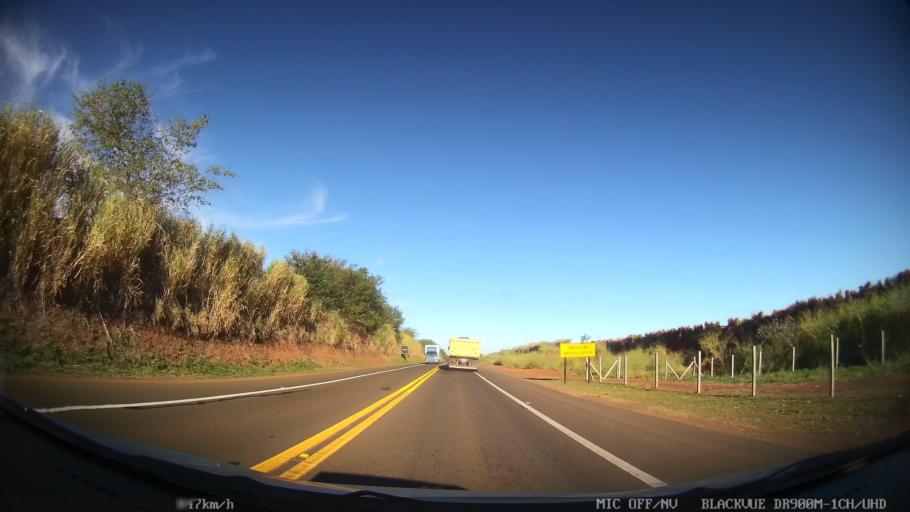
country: BR
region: Sao Paulo
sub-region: Americo Brasiliense
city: Americo Brasiliense
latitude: -21.7609
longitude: -48.1162
